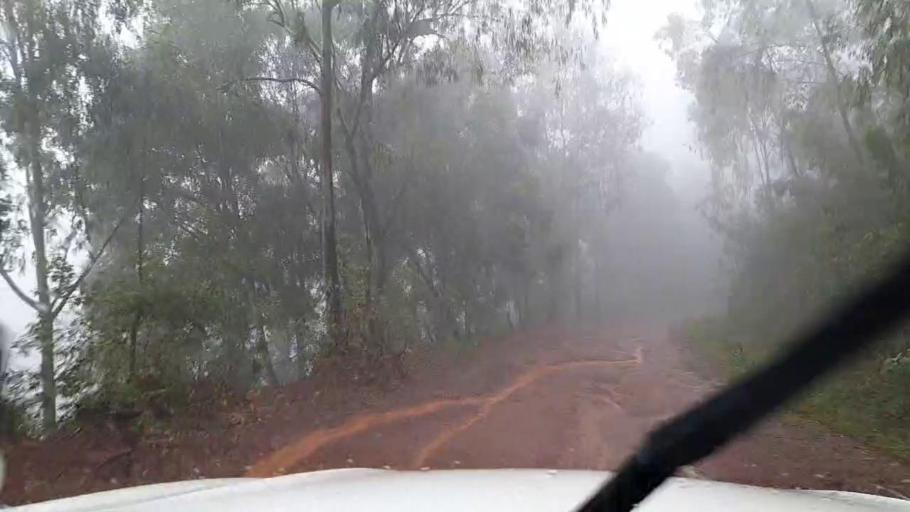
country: RW
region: Kigali
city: Kigali
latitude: -1.7665
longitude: 29.9941
